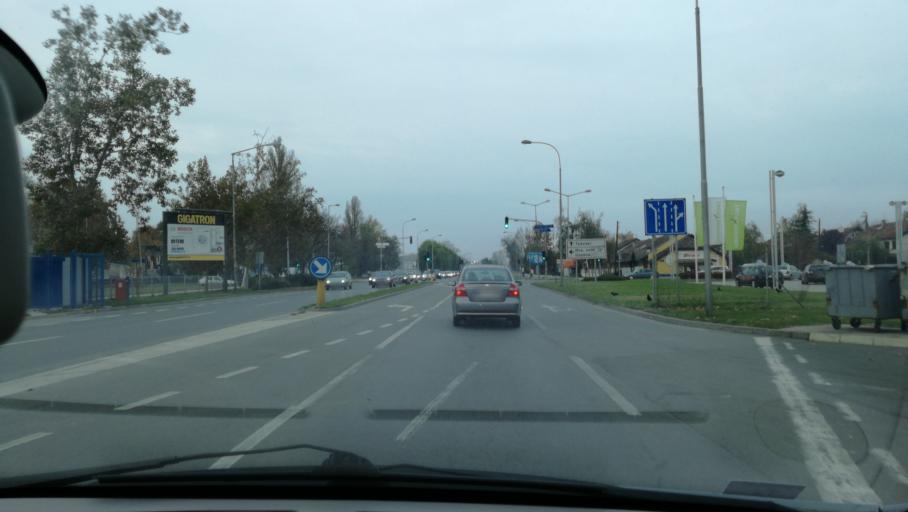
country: RS
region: Autonomna Pokrajina Vojvodina
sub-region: Juznobacki Okrug
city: Novi Sad
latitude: 45.2724
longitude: 19.8307
